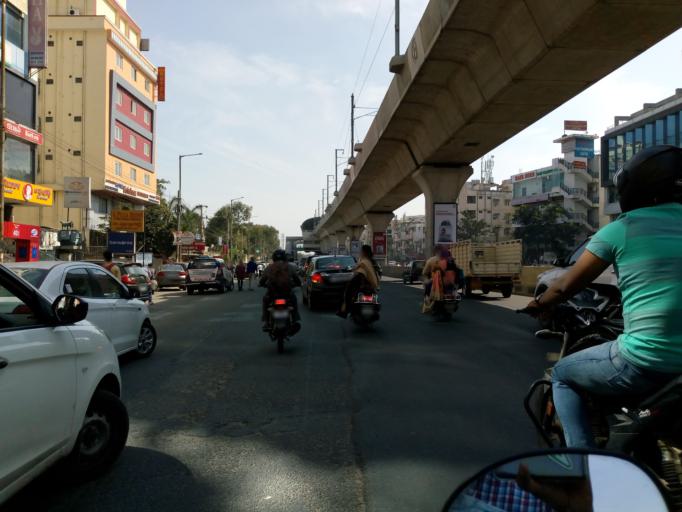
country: IN
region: Telangana
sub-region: Rangareddi
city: Uppal Kalan
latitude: 17.4168
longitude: 78.5441
